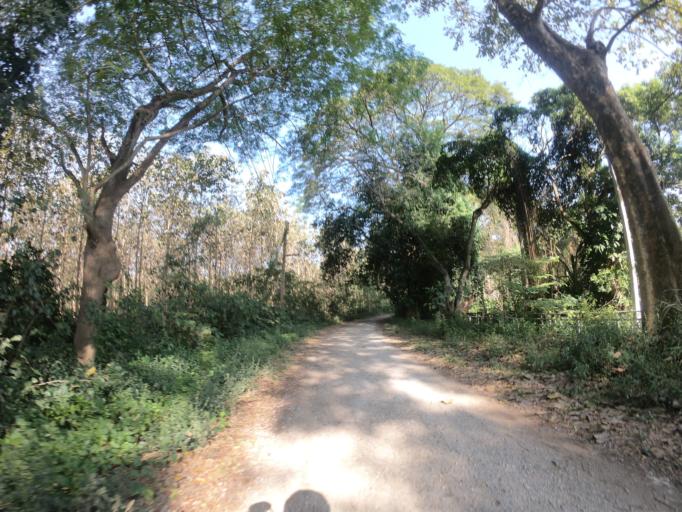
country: TH
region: Chiang Mai
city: Saraphi
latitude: 18.7361
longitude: 98.9872
